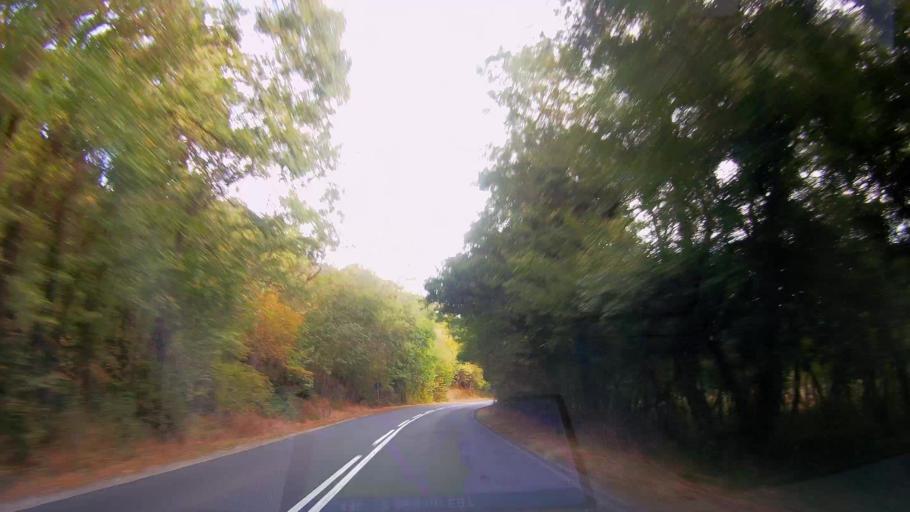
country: BG
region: Burgas
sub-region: Obshtina Primorsko
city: Primorsko
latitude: 42.3094
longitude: 27.7242
